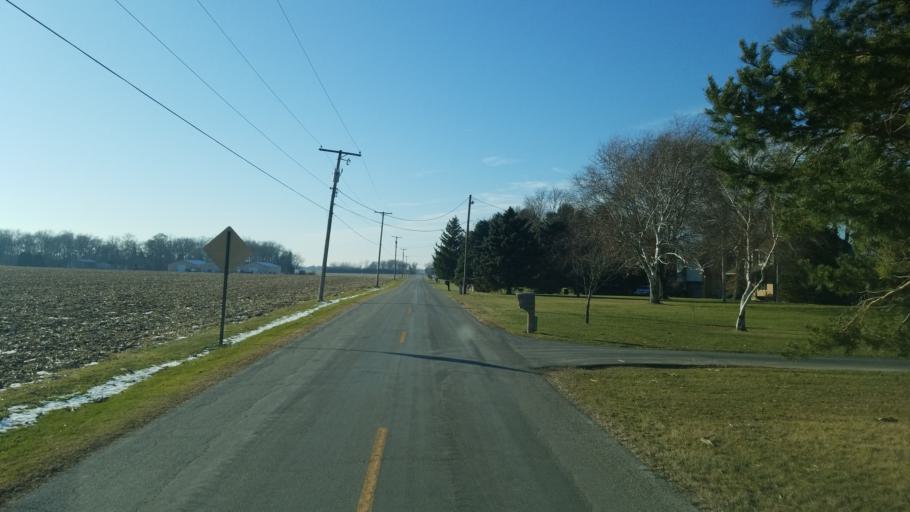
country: US
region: Ohio
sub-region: Huron County
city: Bellevue
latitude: 41.2992
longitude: -82.8805
